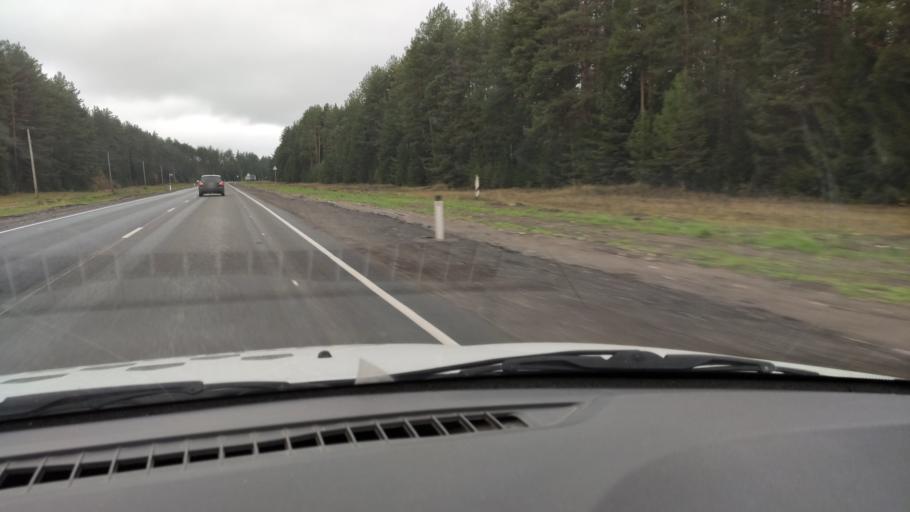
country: RU
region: Kirov
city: Belaya Kholunitsa
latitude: 58.8435
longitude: 50.8065
